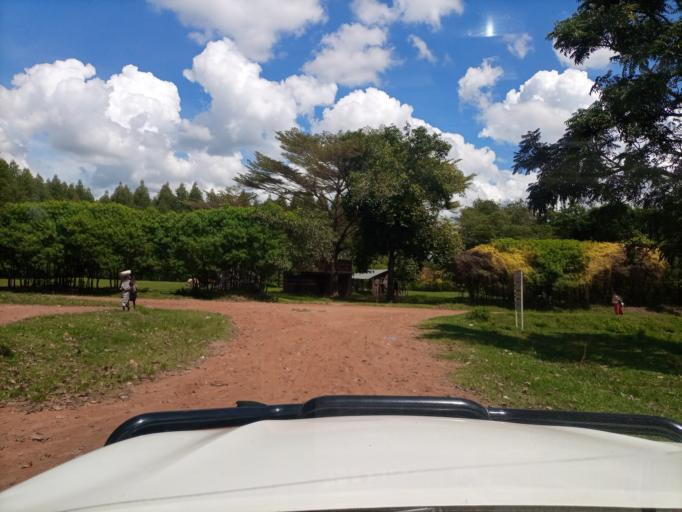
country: UG
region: Eastern Region
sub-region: Tororo District
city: Tororo
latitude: 0.7236
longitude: 34.0167
